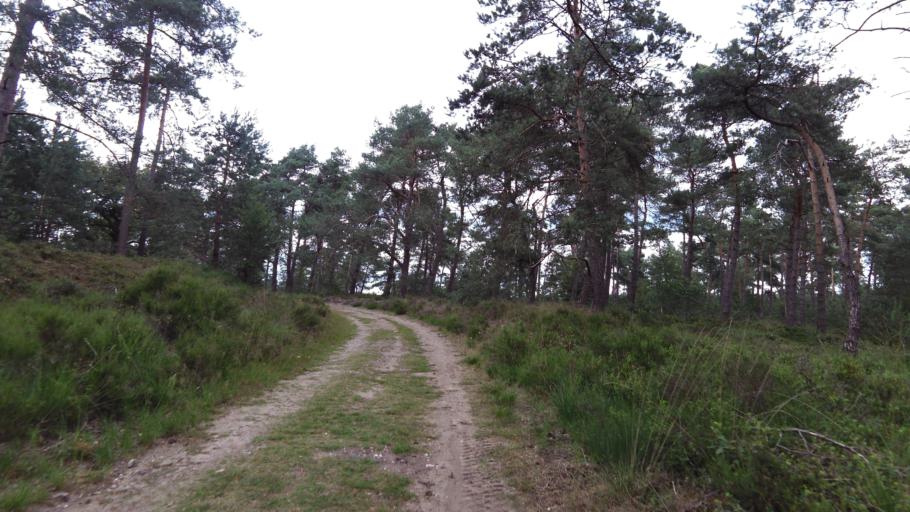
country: NL
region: Gelderland
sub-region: Gemeente Apeldoorn
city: Apeldoorn
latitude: 52.2054
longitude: 5.8698
